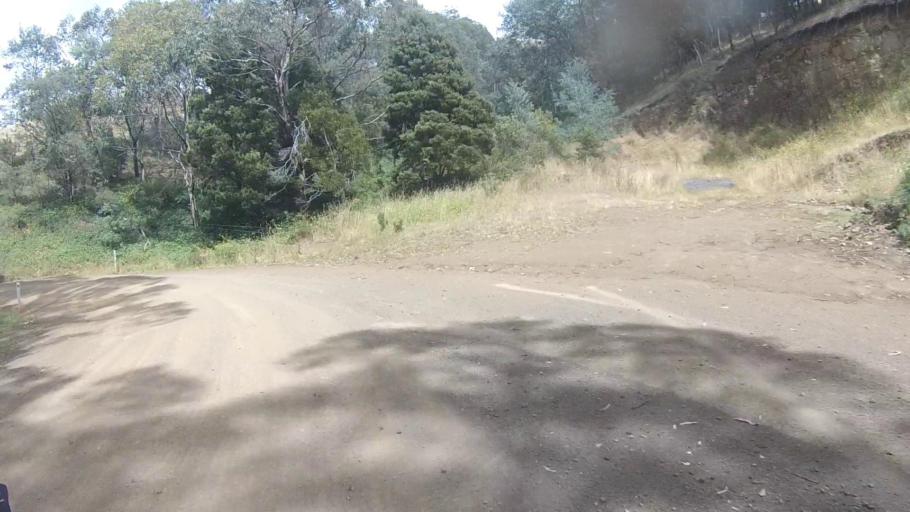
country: AU
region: Tasmania
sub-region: Sorell
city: Sorell
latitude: -42.7870
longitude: 147.8420
